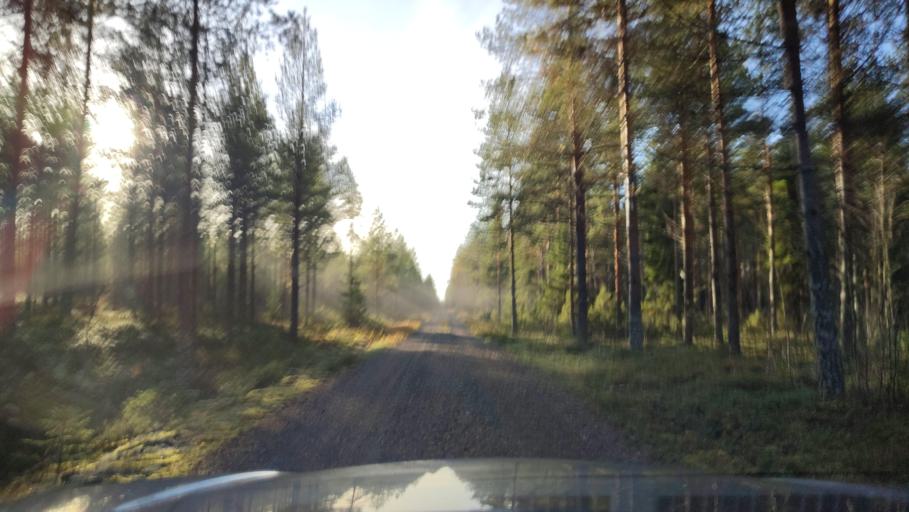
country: FI
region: Southern Ostrobothnia
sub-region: Suupohja
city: Karijoki
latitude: 62.1924
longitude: 21.6067
